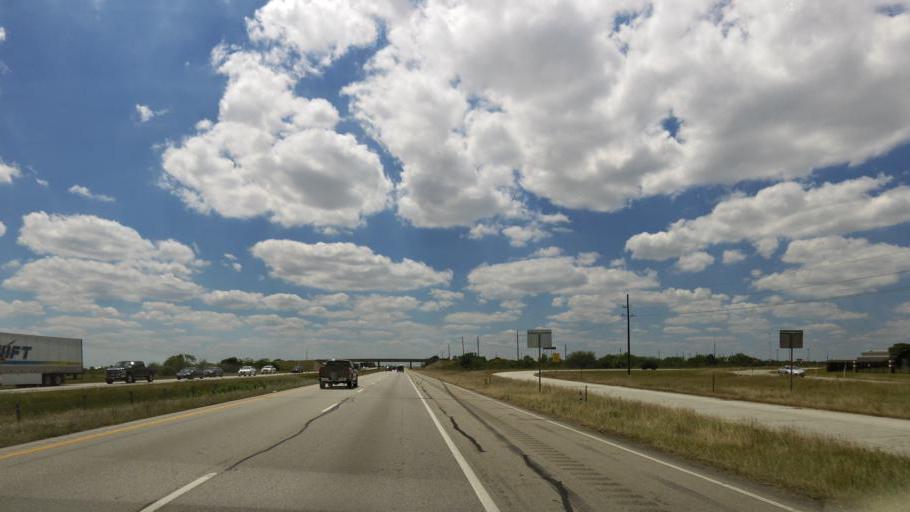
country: US
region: Texas
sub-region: Austin County
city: Sealy
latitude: 29.7594
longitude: -96.2171
